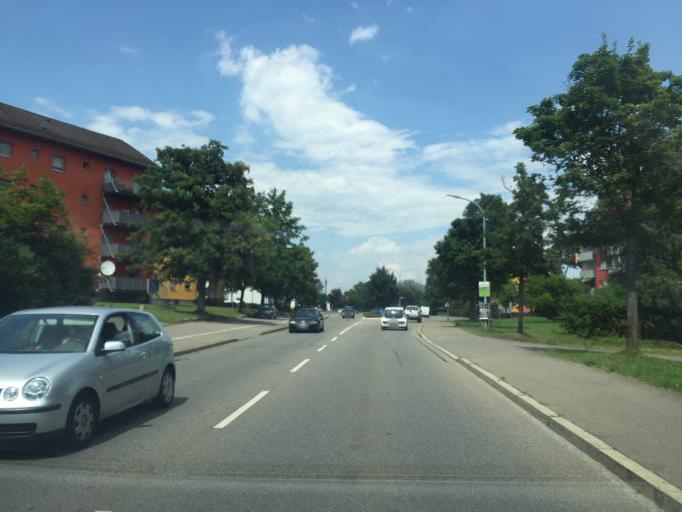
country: DE
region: Baden-Wuerttemberg
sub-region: Freiburg Region
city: Rielasingen-Worblingen
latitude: 47.7411
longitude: 8.8507
